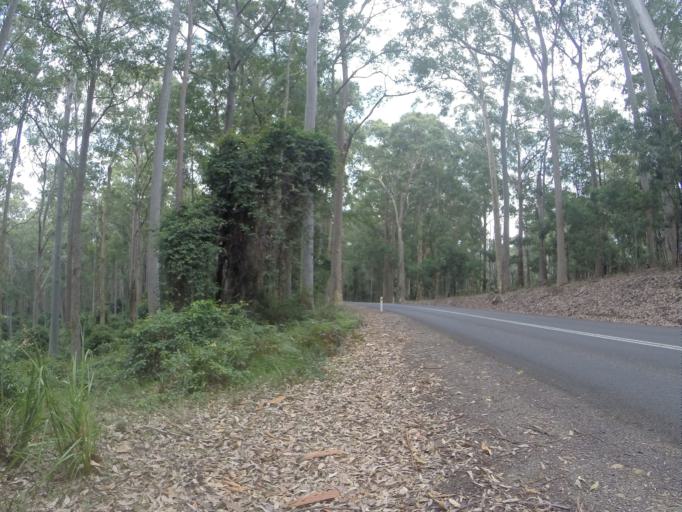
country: AU
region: New South Wales
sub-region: Eurobodalla
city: Batemans Bay
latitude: -35.6561
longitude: 150.2519
